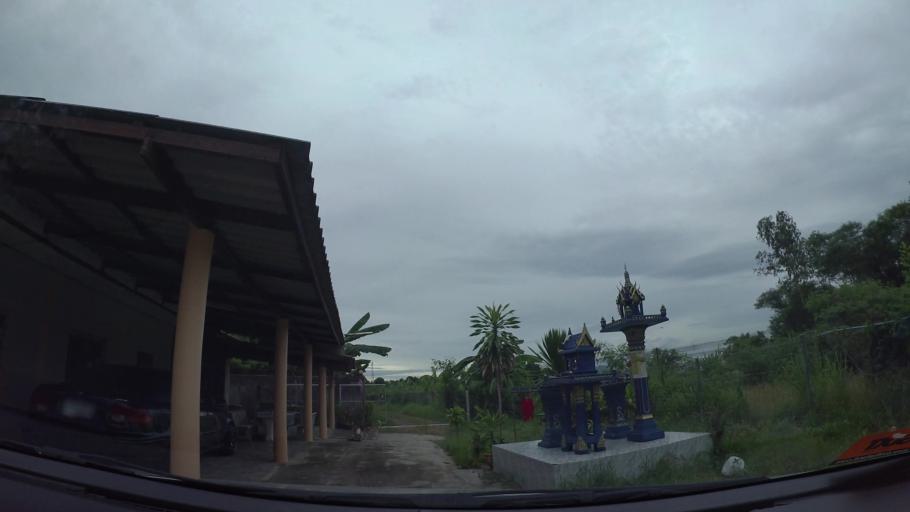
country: TH
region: Chon Buri
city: Si Racha
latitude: 13.1355
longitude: 100.9447
